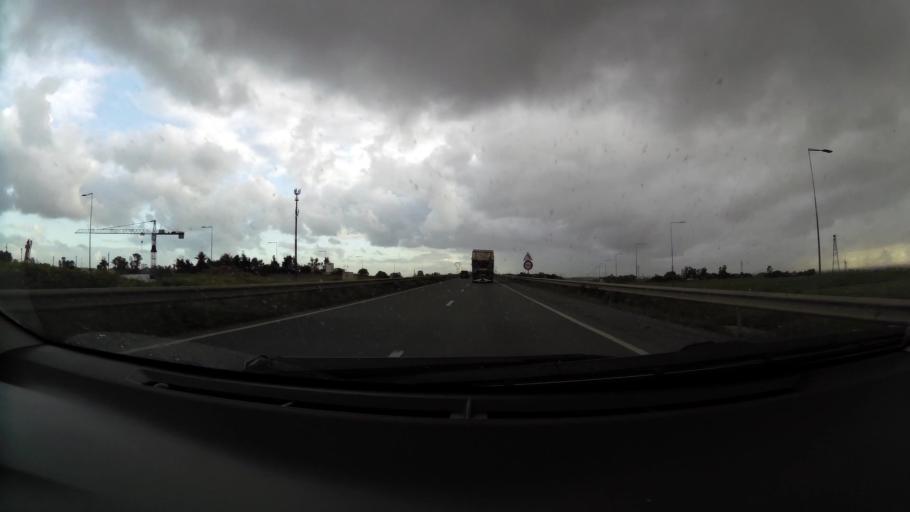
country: MA
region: Grand Casablanca
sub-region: Mohammedia
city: Mohammedia
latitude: 33.6504
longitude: -7.4176
